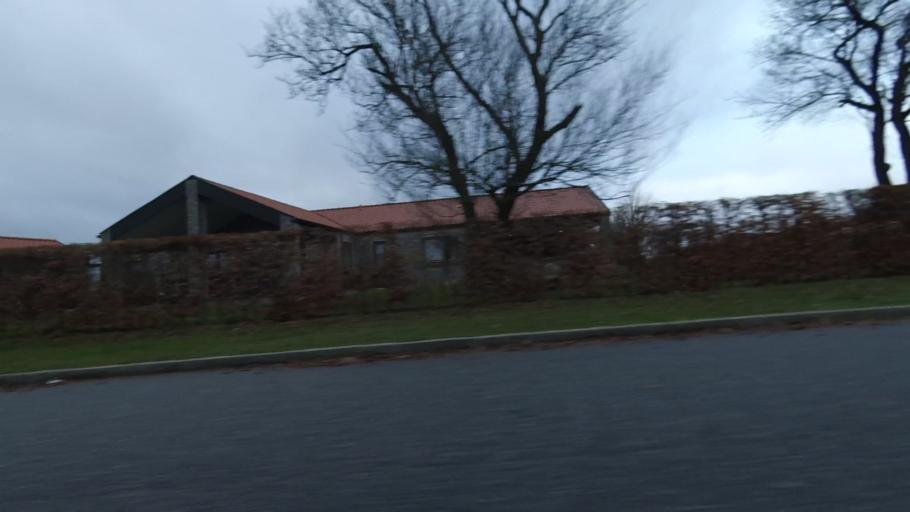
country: DK
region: Central Jutland
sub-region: Arhus Kommune
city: Marslet
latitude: 56.1043
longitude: 10.1782
